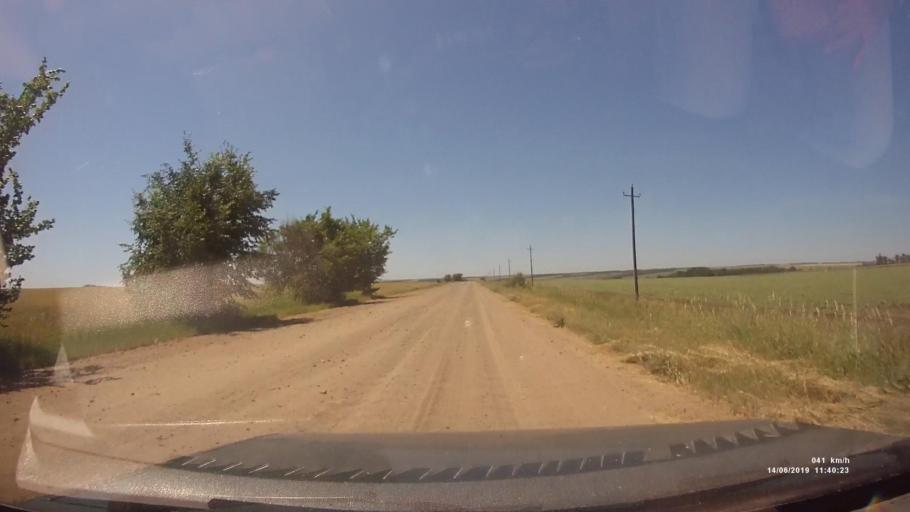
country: RU
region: Rostov
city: Kazanskaya
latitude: 49.8672
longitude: 41.3602
